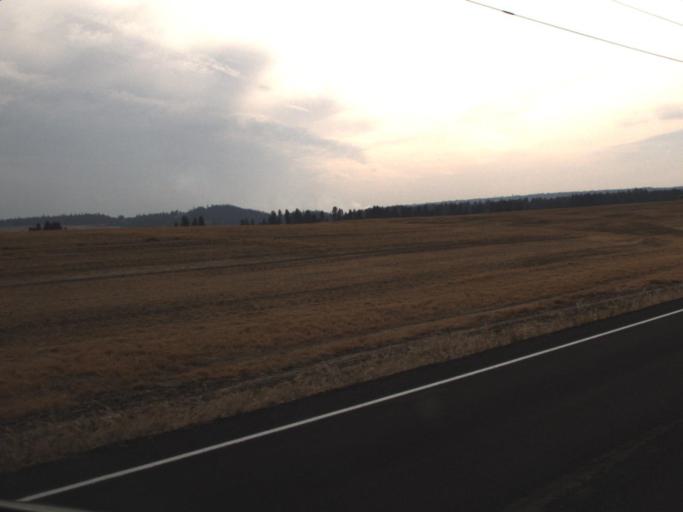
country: US
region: Washington
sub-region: Spokane County
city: Mead
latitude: 47.7876
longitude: -117.2971
